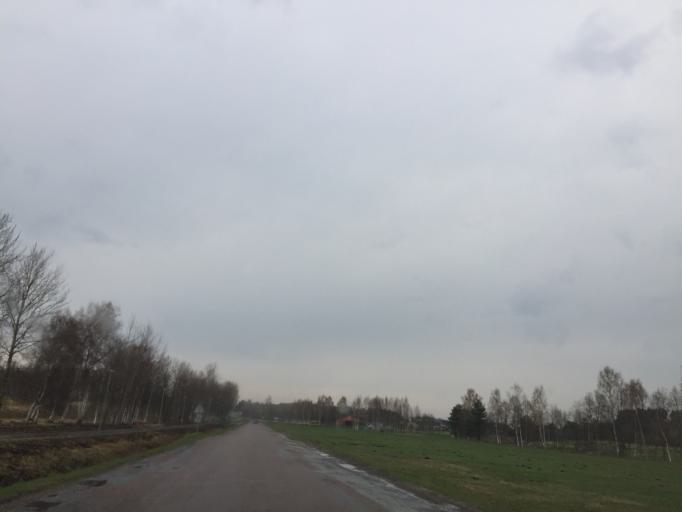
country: EE
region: Tartu
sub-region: UElenurme vald
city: Ulenurme
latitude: 58.3016
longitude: 26.7248
